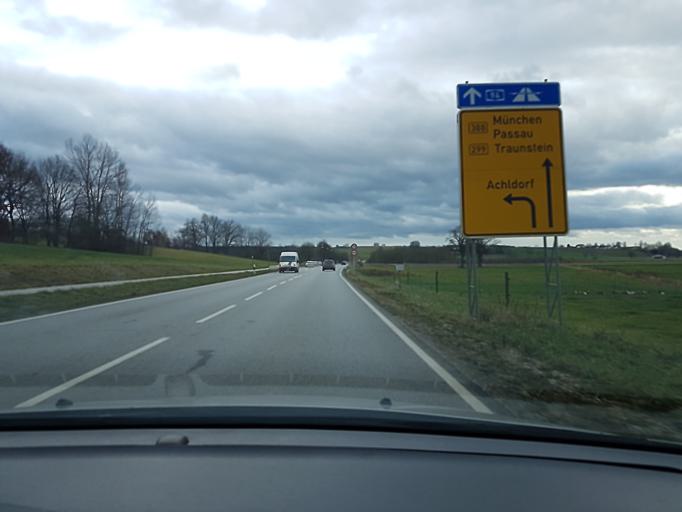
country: DE
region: Bavaria
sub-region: Lower Bavaria
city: Vilsbiburg
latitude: 48.4338
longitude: 12.3525
